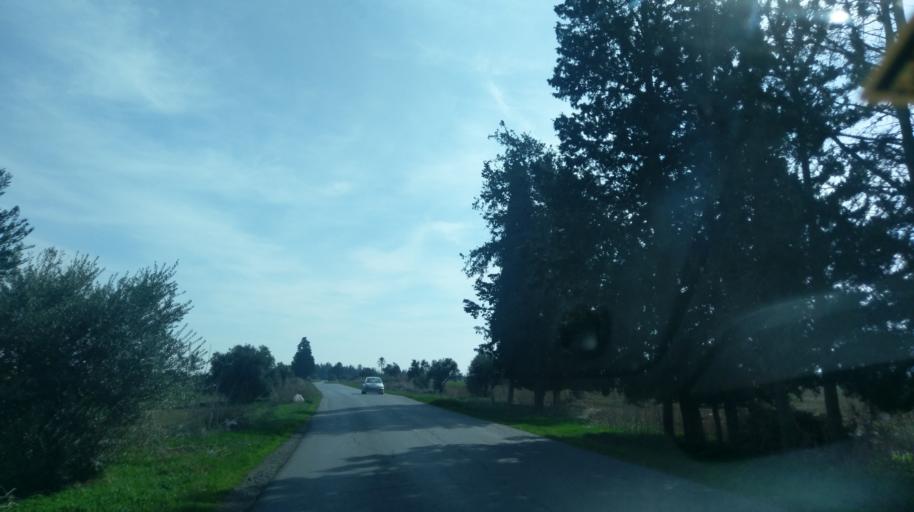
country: CY
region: Larnaka
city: Troulloi
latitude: 35.1516
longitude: 33.6301
